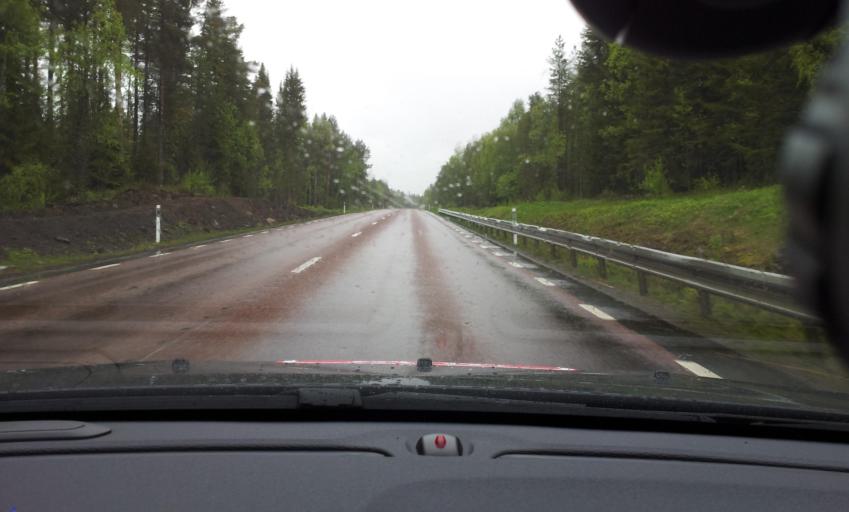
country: SE
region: Jaemtland
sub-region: Bergs Kommun
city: Hoverberg
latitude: 62.9422
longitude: 14.5430
